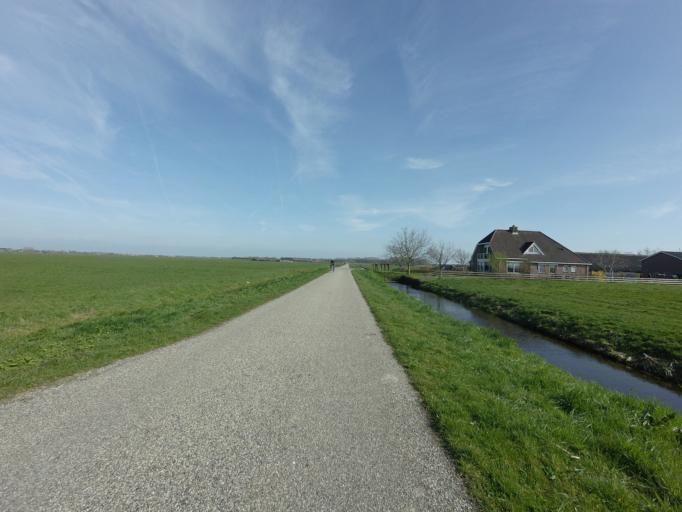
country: NL
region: South Holland
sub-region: Bodegraven-Reeuwijk
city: Bodegraven
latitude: 52.0684
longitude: 4.7973
